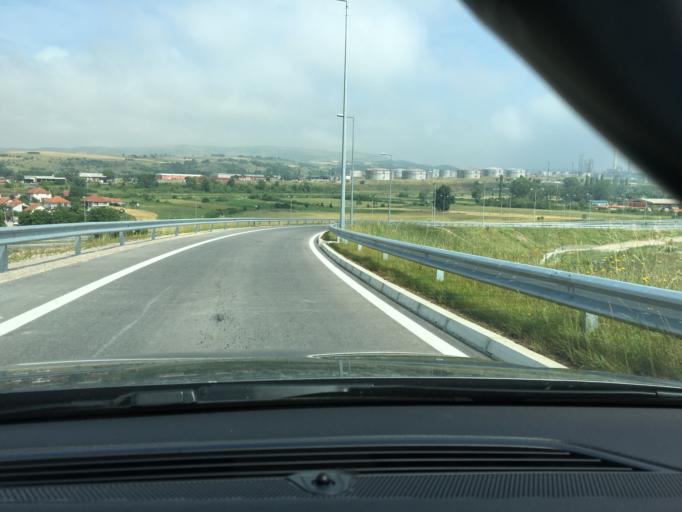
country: MK
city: Miladinovci
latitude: 41.9887
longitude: 21.6587
